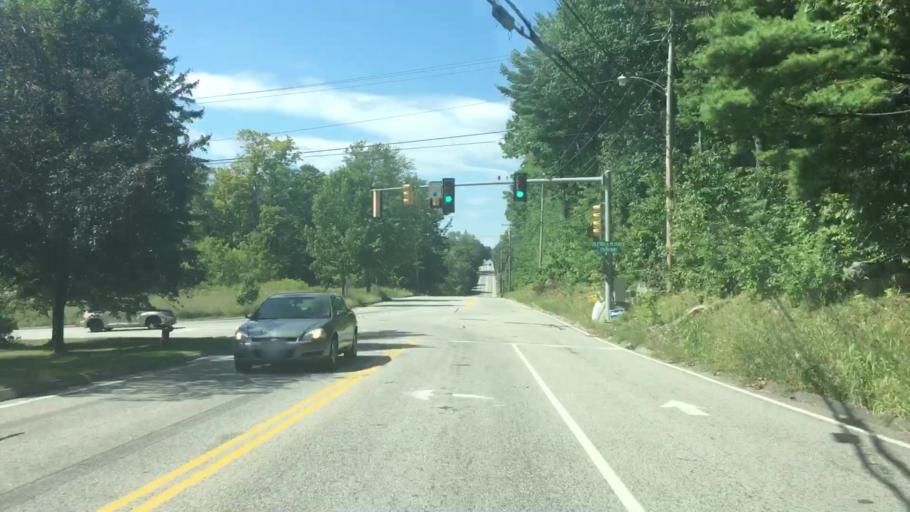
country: US
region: Maine
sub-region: Androscoggin County
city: Lewiston
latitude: 44.0849
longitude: -70.1759
